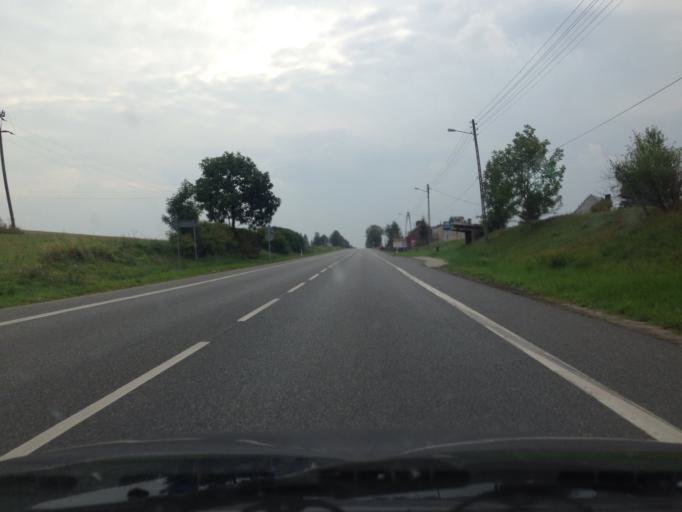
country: PL
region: Kujawsko-Pomorskie
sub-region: Powiat swiecki
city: Nowe
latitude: 53.6739
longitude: 18.7253
